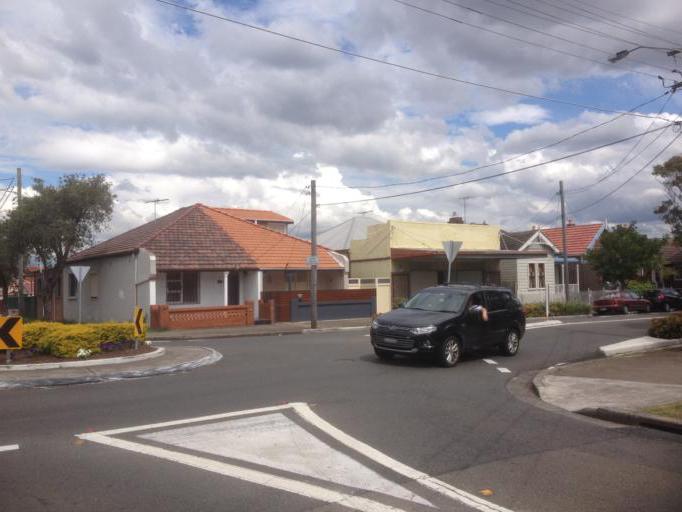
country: AU
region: New South Wales
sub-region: Botany Bay
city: Mascot
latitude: -33.9259
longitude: 151.1982
